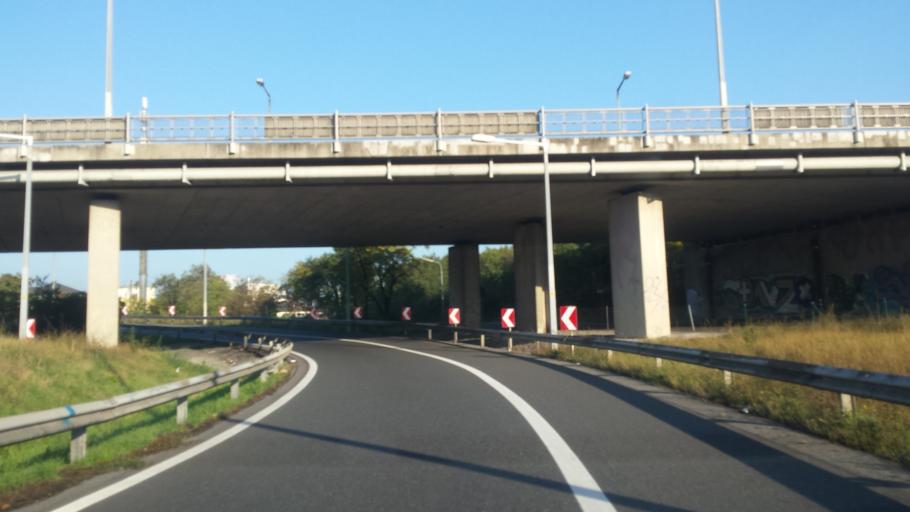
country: AT
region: Vienna
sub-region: Wien Stadt
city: Vienna
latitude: 48.2401
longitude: 16.4036
